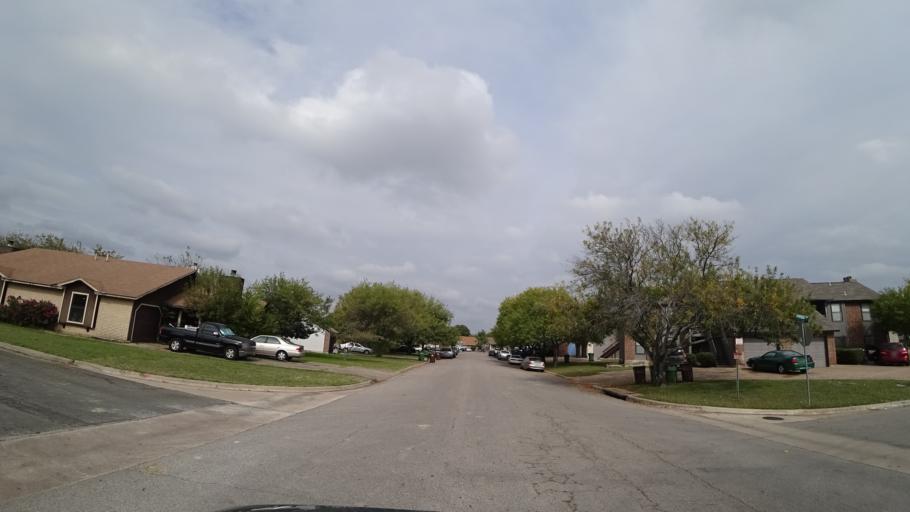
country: US
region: Texas
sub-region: Williamson County
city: Round Rock
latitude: 30.4920
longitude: -97.6810
